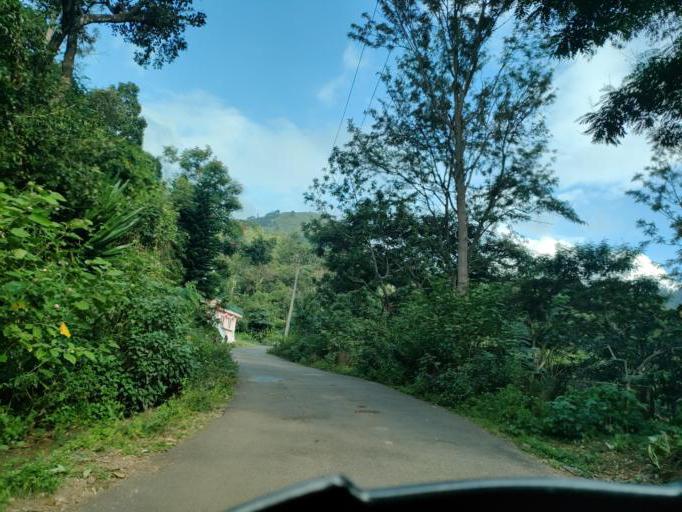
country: IN
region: Tamil Nadu
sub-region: Dindigul
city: Kodaikanal
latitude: 10.2792
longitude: 77.5299
